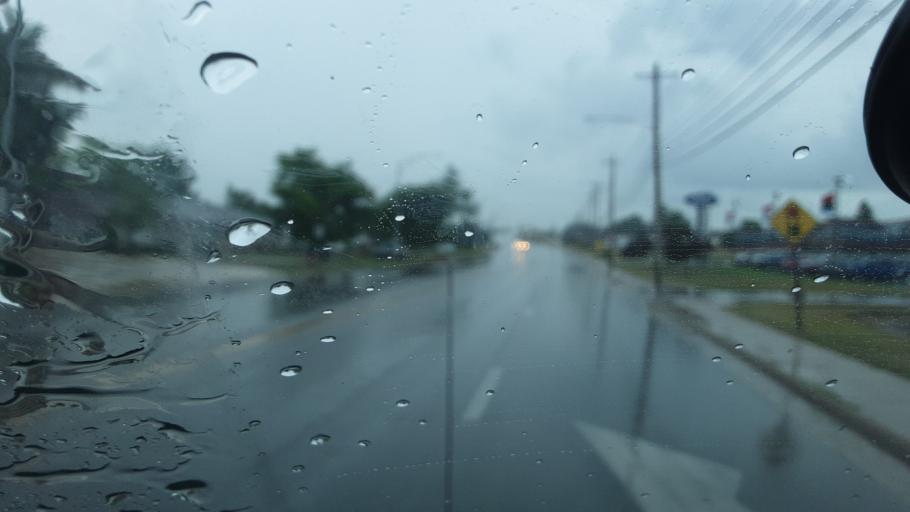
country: US
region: Ohio
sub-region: Williams County
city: Montpelier
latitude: 41.5865
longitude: -84.5914
